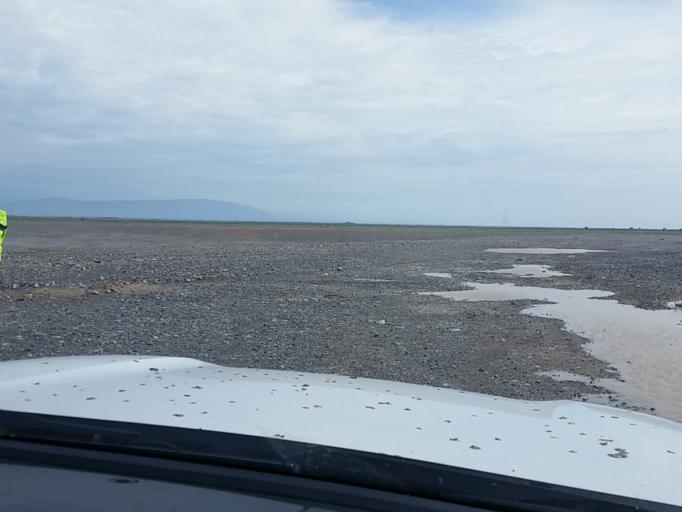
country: KZ
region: Almaty Oblysy
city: Saryozek
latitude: 43.6580
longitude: 78.4409
